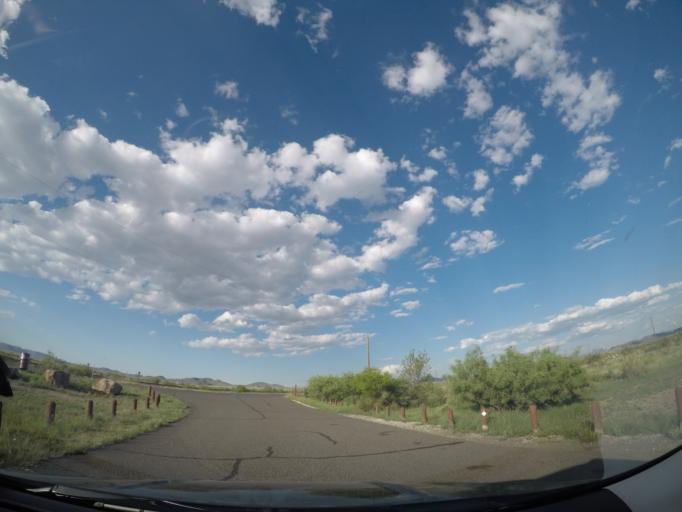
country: US
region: Texas
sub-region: Presidio County
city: Marfa
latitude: 30.2754
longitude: -103.8819
